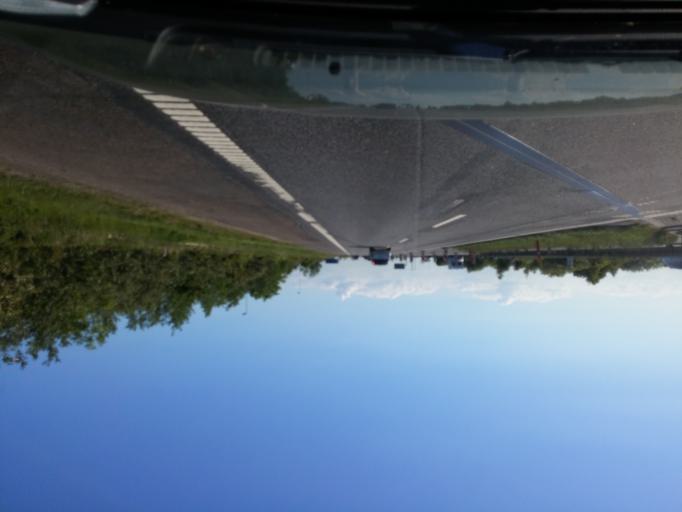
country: DK
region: South Denmark
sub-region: Middelfart Kommune
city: Norre Aby
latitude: 55.4689
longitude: 9.8978
